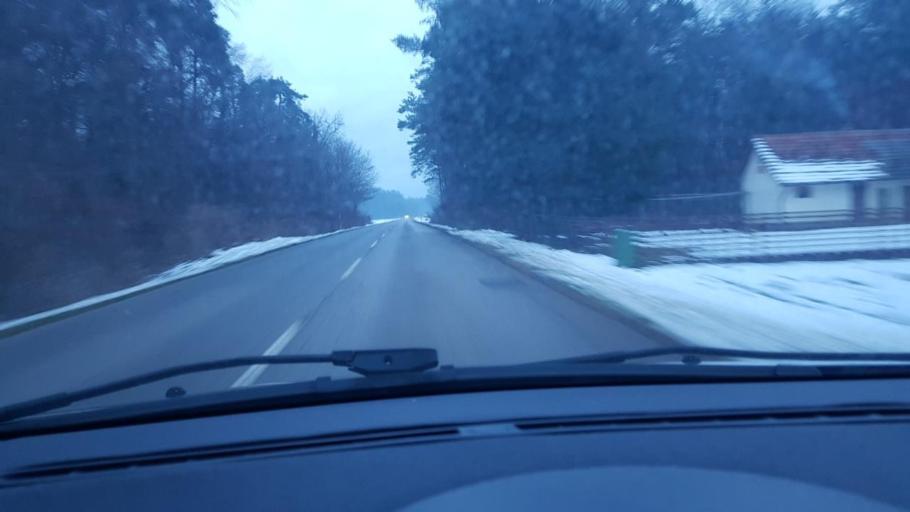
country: SI
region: Kidricevo
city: Kidricevo
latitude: 46.3894
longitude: 15.8038
